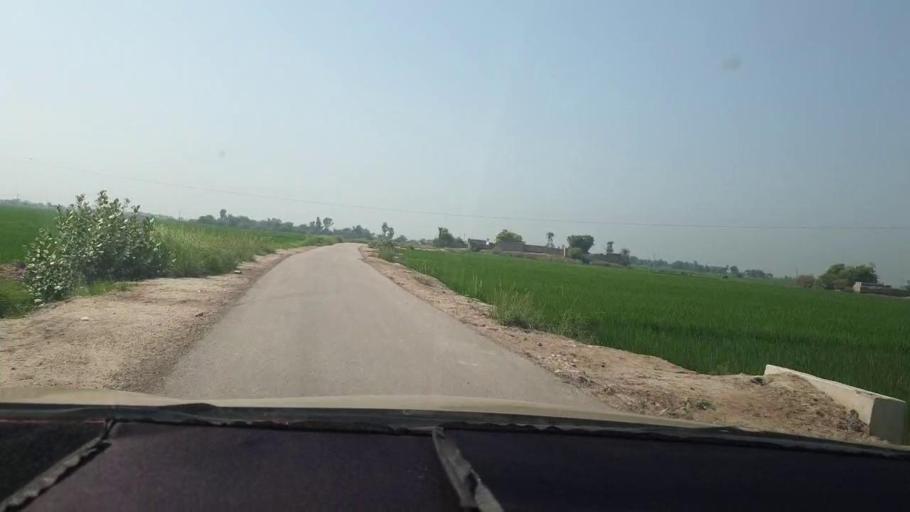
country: PK
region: Sindh
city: Kambar
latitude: 27.5635
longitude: 68.0443
